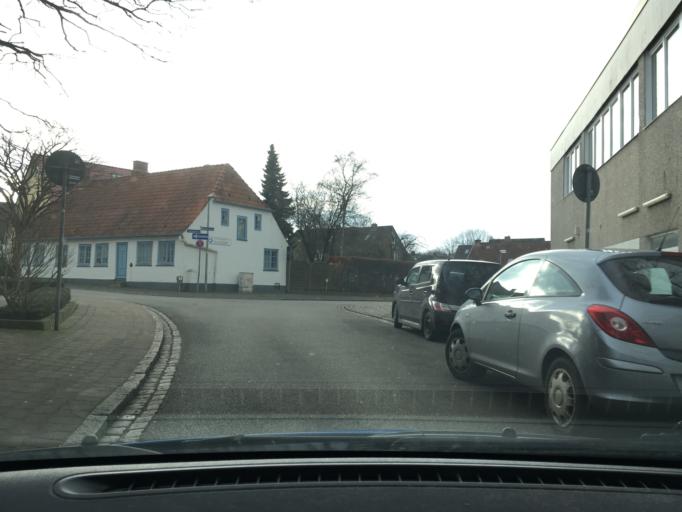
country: DE
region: Schleswig-Holstein
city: Wedel
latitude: 53.5774
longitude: 9.7048
